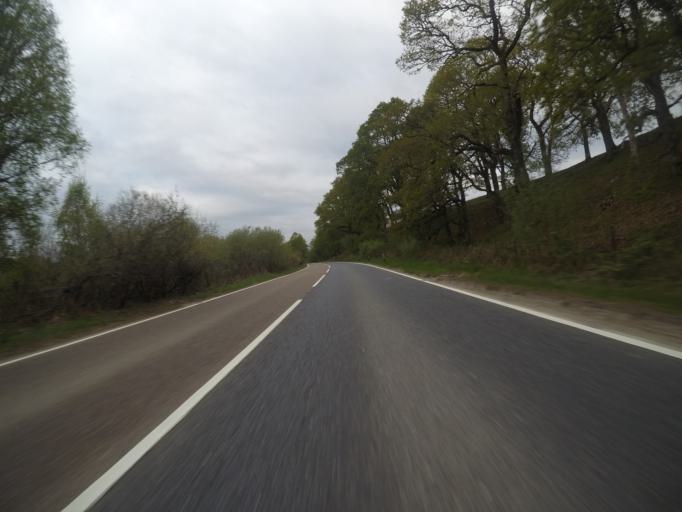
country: GB
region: Scotland
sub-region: Highland
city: Spean Bridge
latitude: 56.8946
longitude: -4.8917
